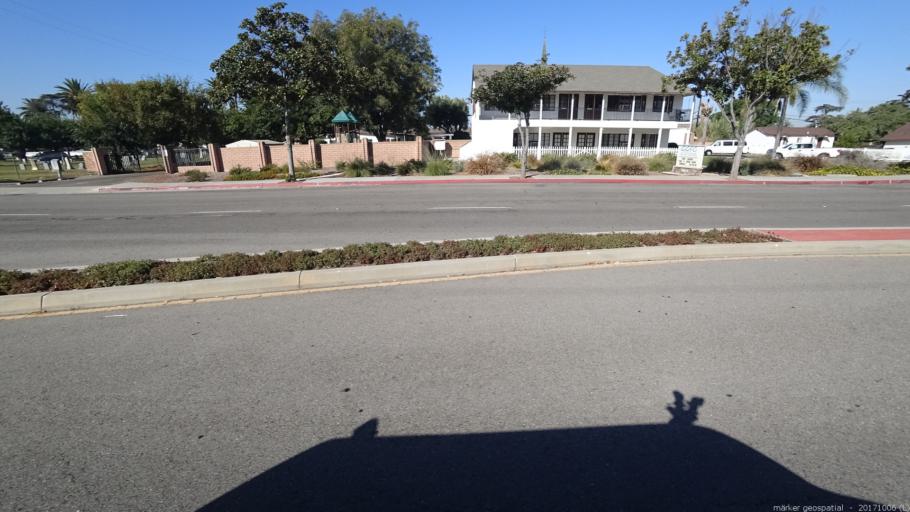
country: US
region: California
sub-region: Orange County
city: Stanton
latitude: 33.7850
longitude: -117.9752
